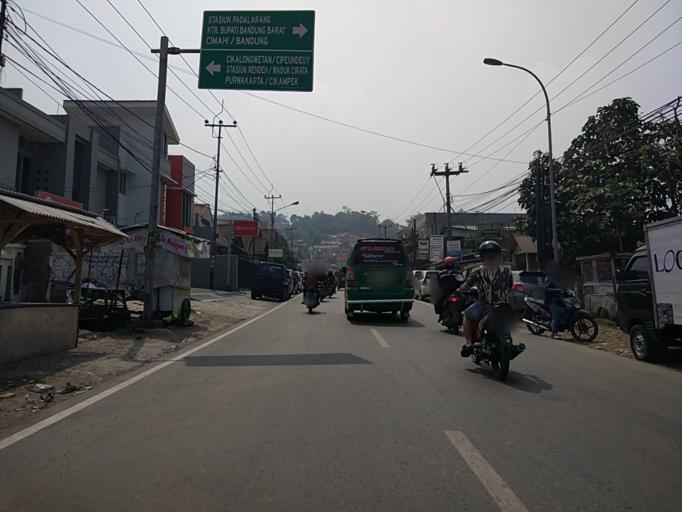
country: ID
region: West Java
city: Padalarang
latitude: -6.8378
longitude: 107.4881
